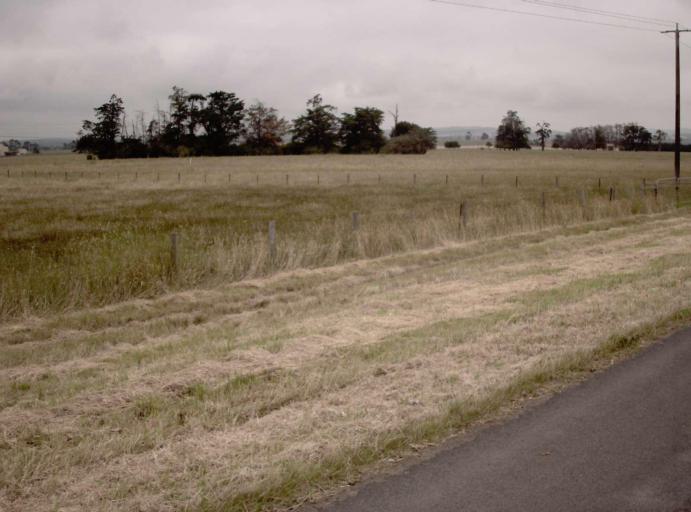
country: AU
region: Victoria
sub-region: Latrobe
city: Morwell
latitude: -38.2650
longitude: 146.4228
